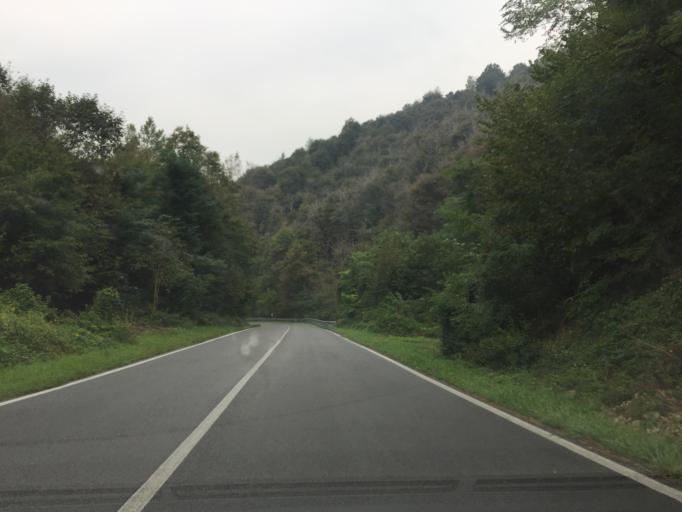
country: IT
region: Piedmont
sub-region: Provincia di Cuneo
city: Chiusa di Pesio
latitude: 44.3155
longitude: 7.6914
